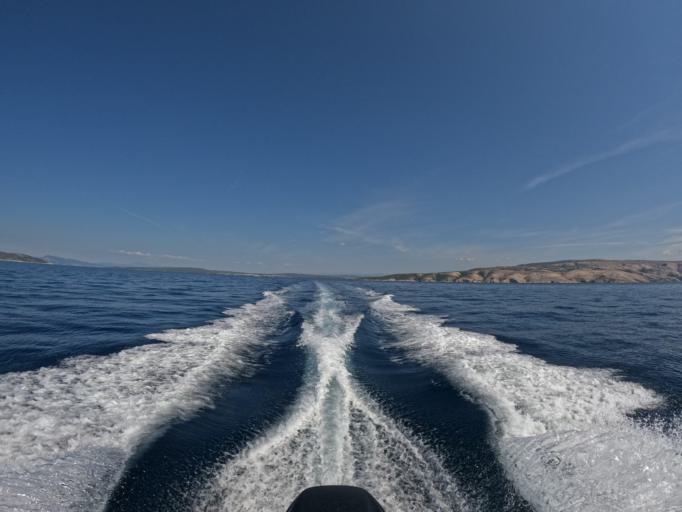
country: HR
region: Primorsko-Goranska
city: Punat
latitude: 44.9413
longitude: 14.6157
